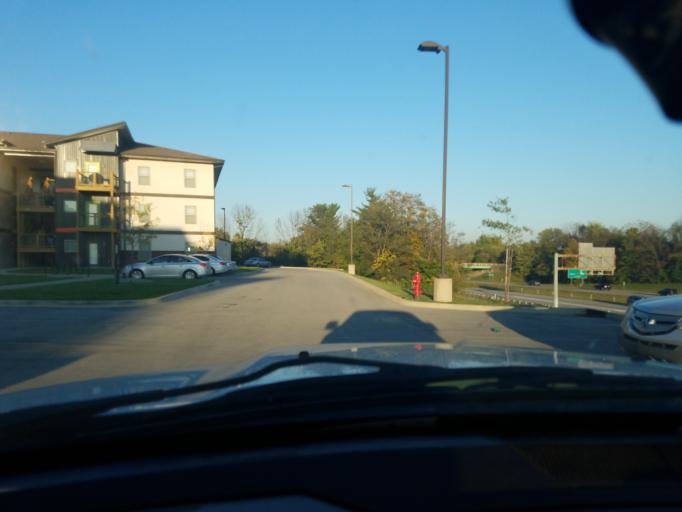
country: US
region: Indiana
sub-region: Floyd County
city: New Albany
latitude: 38.3388
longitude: -85.8141
